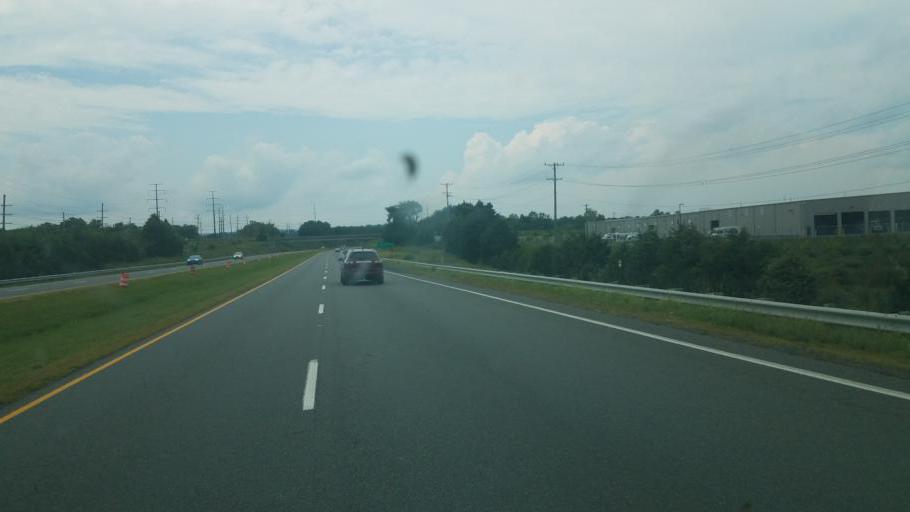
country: US
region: Virginia
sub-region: Frederick County
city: Stephens City
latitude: 39.1258
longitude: -78.2003
